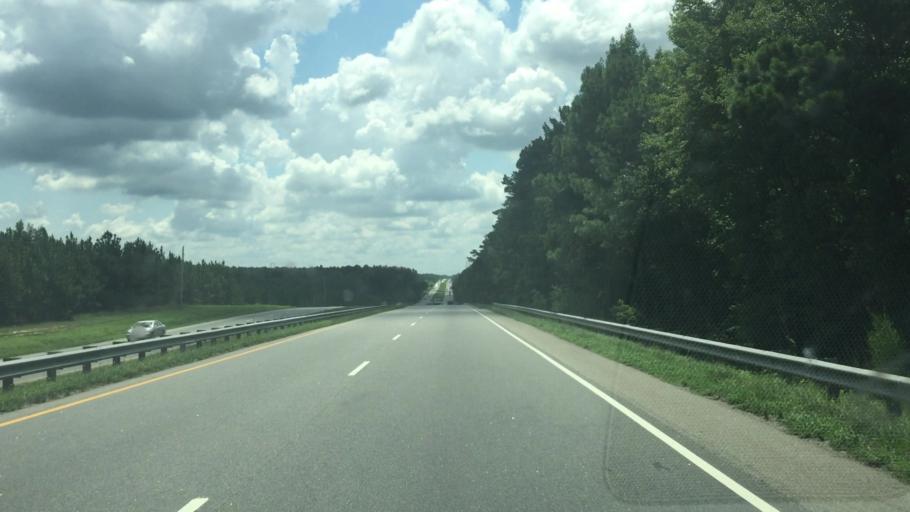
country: US
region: North Carolina
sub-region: Richmond County
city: Hamlet
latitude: 34.8616
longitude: -79.6338
